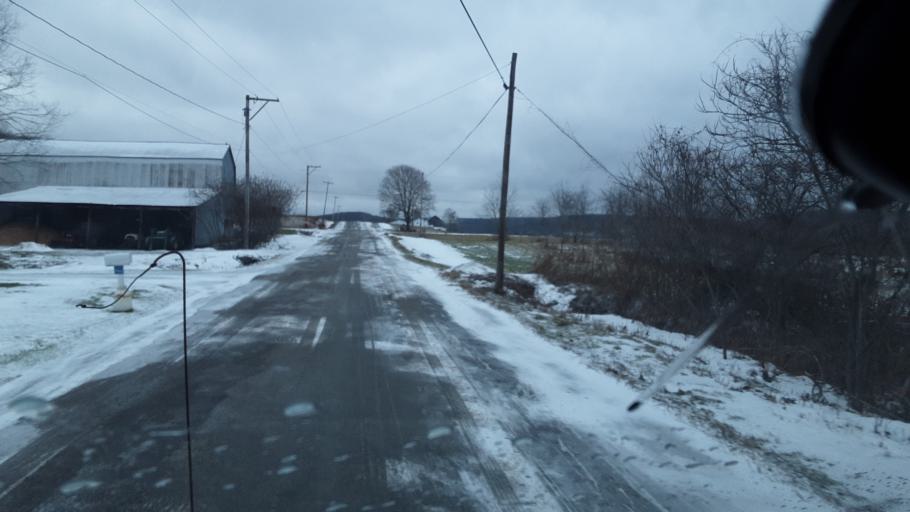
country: US
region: New York
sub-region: Allegany County
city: Friendship
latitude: 42.2938
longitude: -78.1607
